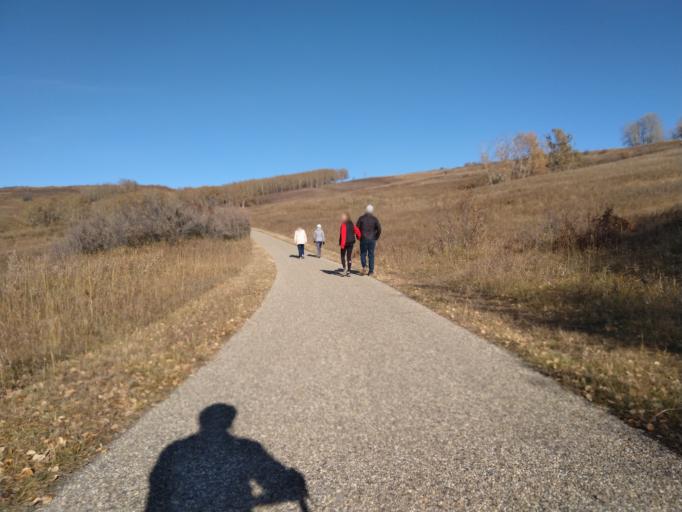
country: CA
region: Alberta
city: Calgary
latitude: 51.1039
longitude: -114.1168
